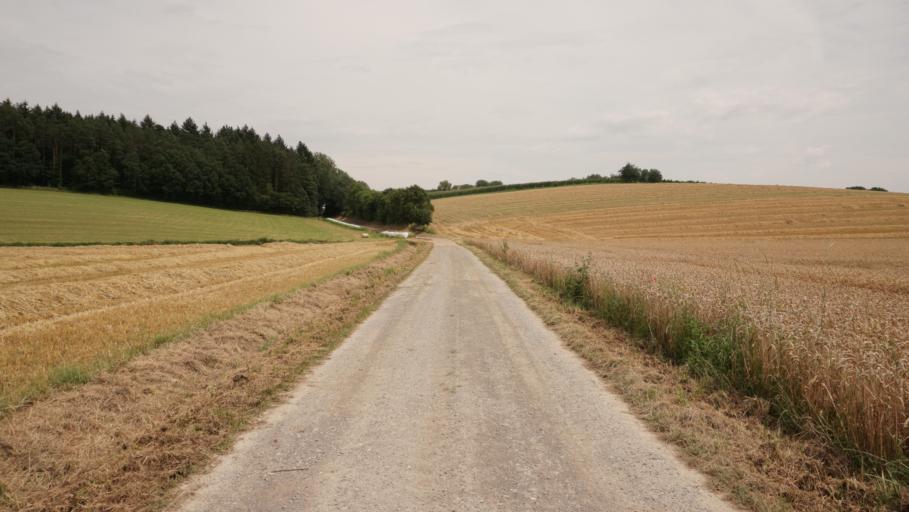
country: DE
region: Baden-Wuerttemberg
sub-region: Karlsruhe Region
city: Billigheim
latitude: 49.3251
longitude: 9.2054
